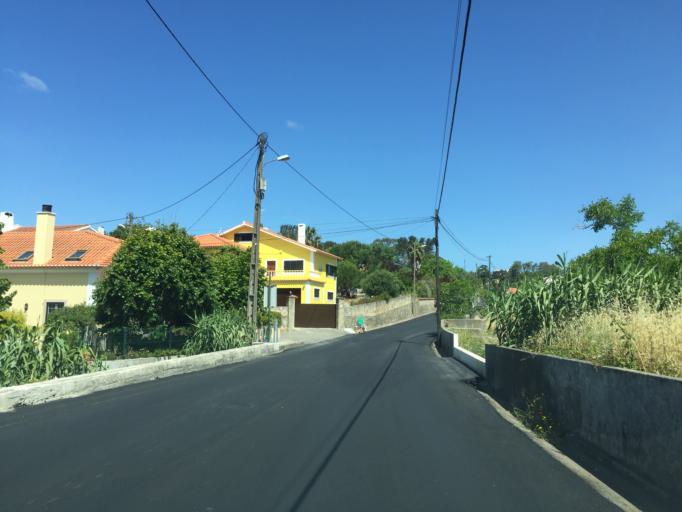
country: PT
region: Lisbon
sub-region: Sintra
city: Sintra
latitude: 38.8077
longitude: -9.4010
